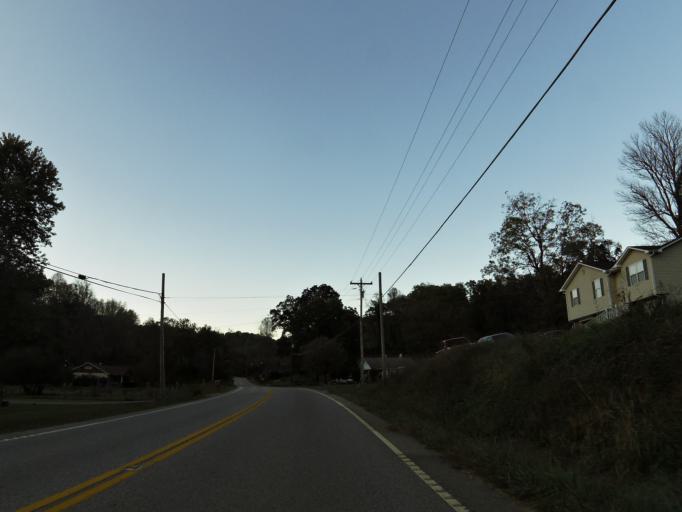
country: US
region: Tennessee
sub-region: Campbell County
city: Caryville
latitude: 36.2639
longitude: -84.1870
